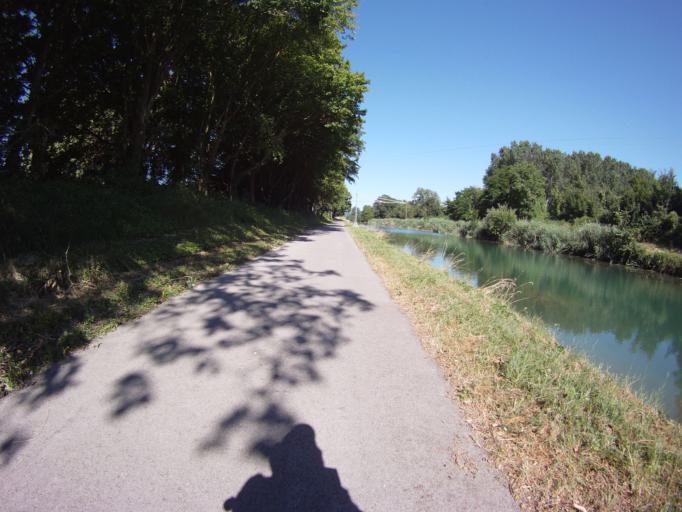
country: FR
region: Champagne-Ardenne
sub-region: Departement de la Marne
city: Ay
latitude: 49.0548
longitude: 3.9890
